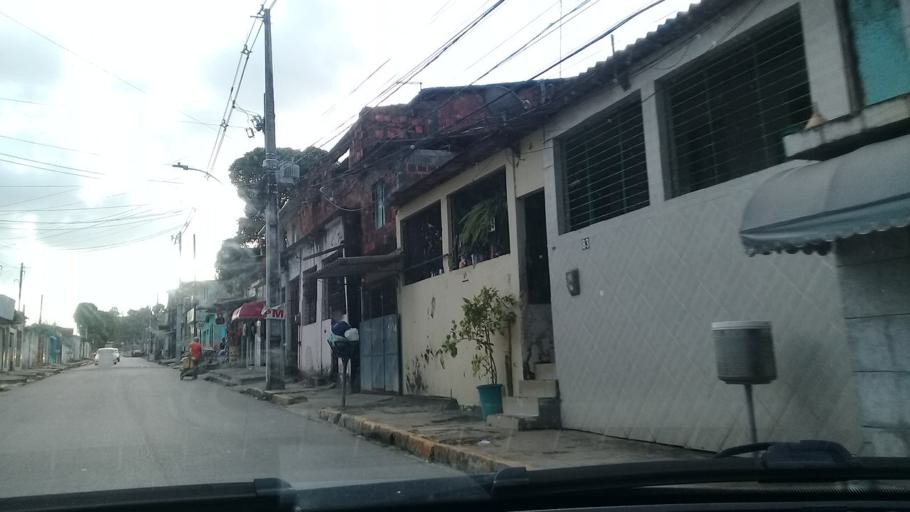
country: BR
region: Pernambuco
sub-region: Jaboatao Dos Guararapes
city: Jaboatao
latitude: -8.1370
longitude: -34.9388
